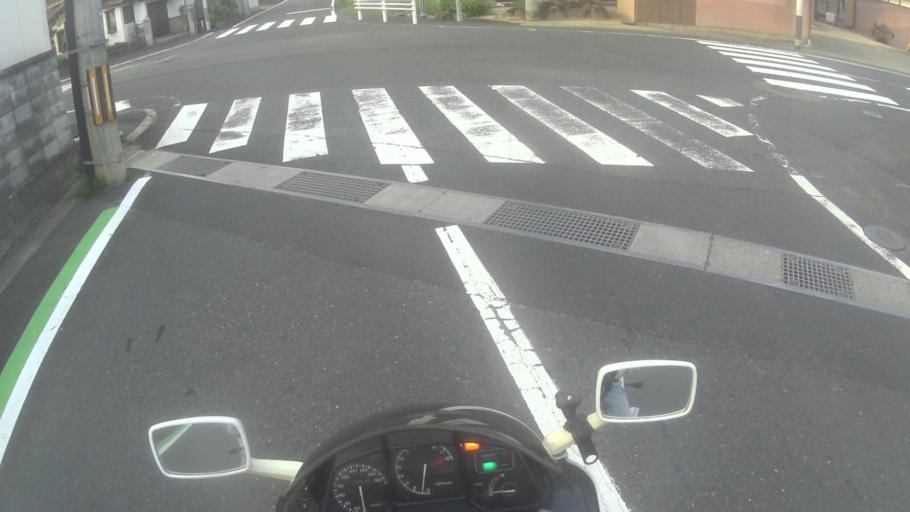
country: JP
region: Kyoto
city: Miyazu
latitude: 35.5305
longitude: 135.0909
